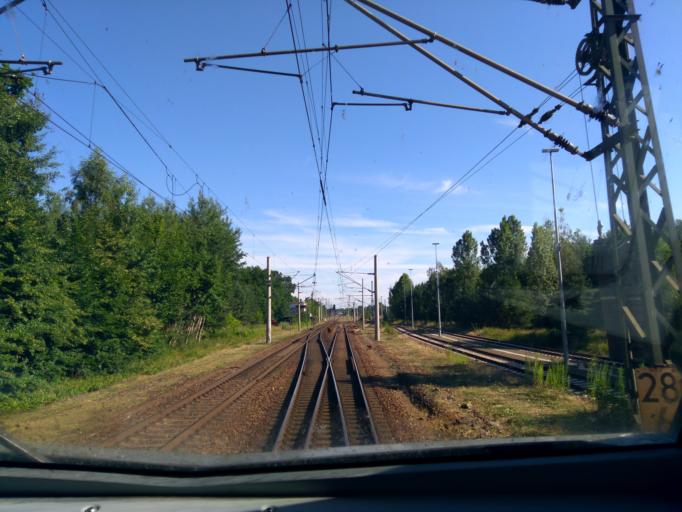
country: DE
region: Brandenburg
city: Konigs Wusterhausen
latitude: 52.2883
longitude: 13.6315
